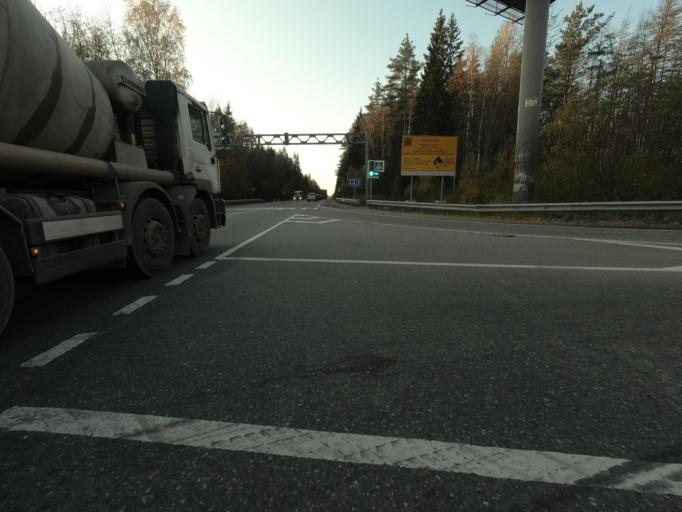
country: RU
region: St.-Petersburg
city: Pesochnyy
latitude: 60.1822
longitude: 30.1294
